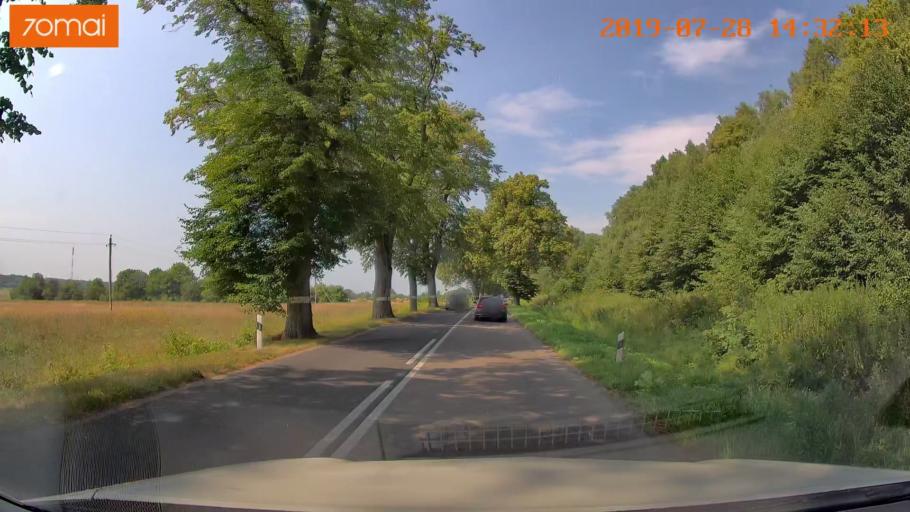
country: RU
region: Kaliningrad
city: Primorsk
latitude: 54.8113
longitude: 20.0437
